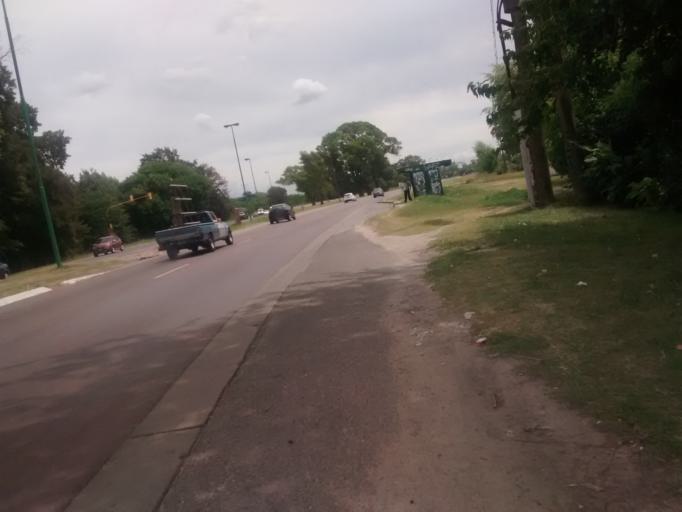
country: AR
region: Buenos Aires
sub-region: Partido de La Plata
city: La Plata
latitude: -34.8617
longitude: -58.0599
